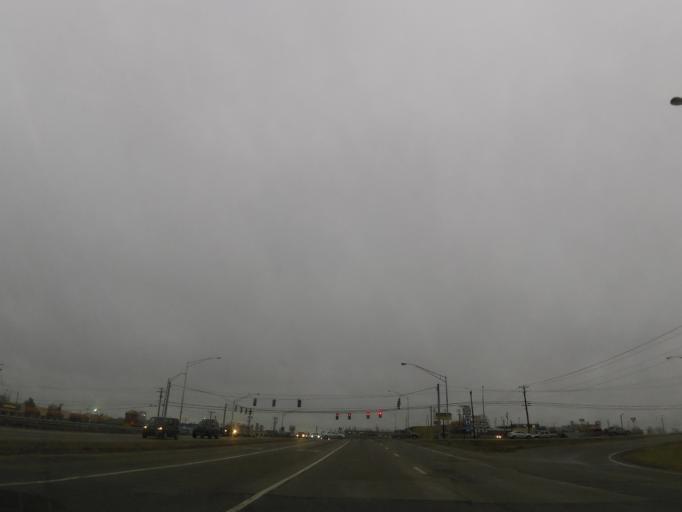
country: US
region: Kentucky
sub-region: Boyle County
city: Danville
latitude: 37.6174
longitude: -84.7758
